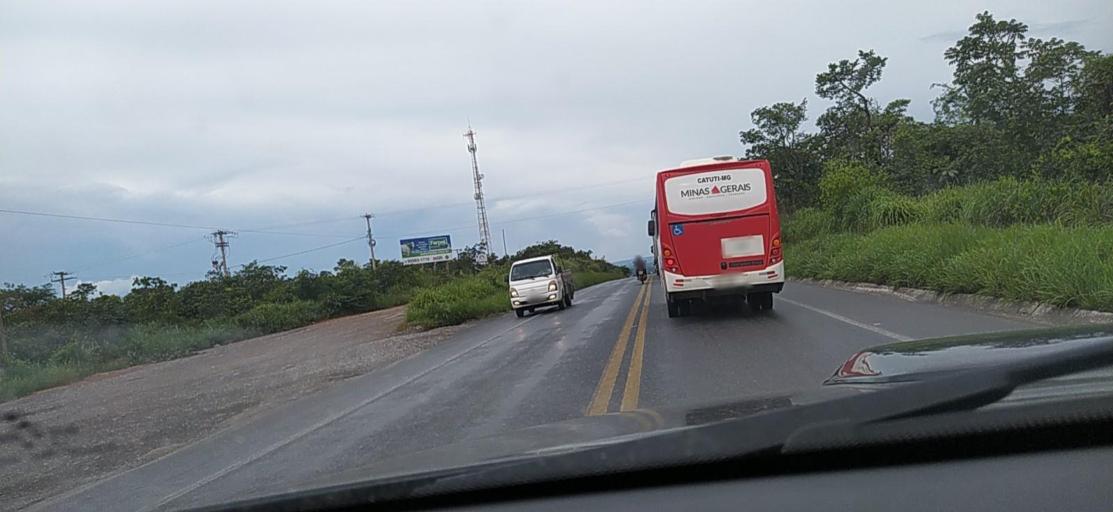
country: BR
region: Minas Gerais
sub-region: Montes Claros
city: Montes Claros
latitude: -16.6625
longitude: -43.7677
